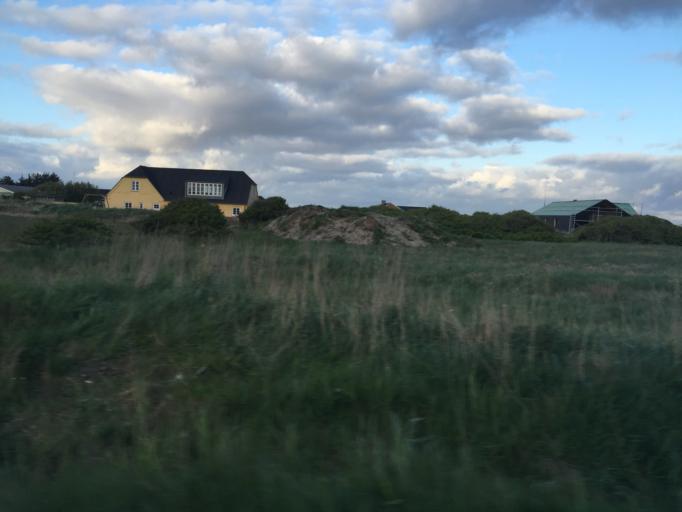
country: DK
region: Central Jutland
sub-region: Ringkobing-Skjern Kommune
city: Hvide Sande
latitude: 56.0513
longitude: 8.1194
